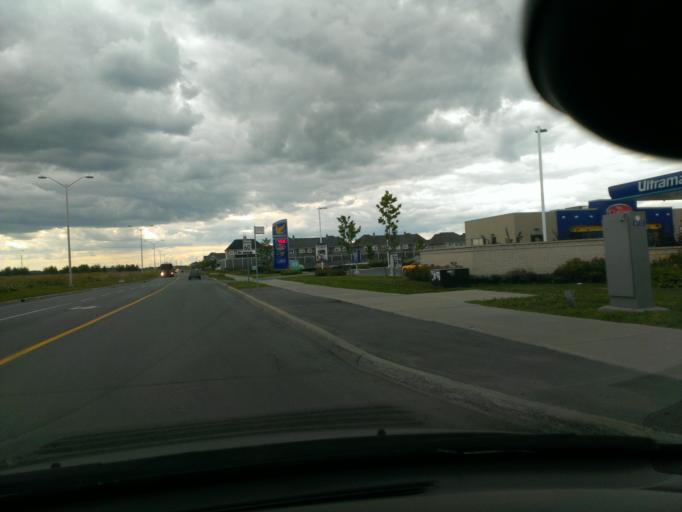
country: CA
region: Ontario
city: Clarence-Rockland
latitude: 45.4506
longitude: -75.4823
